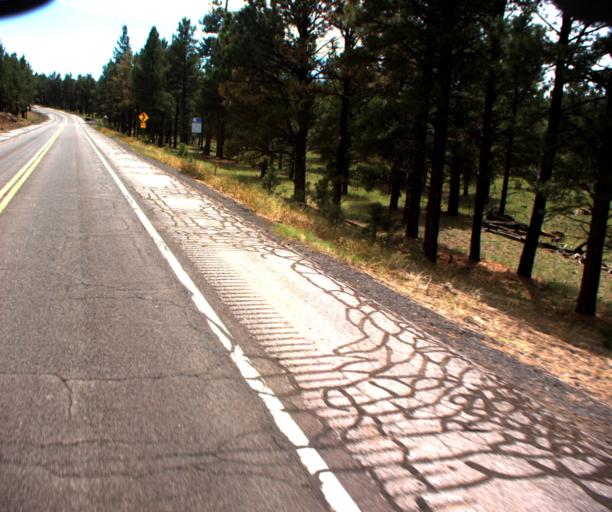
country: US
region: Arizona
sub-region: Coconino County
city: Parks
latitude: 35.4357
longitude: -111.7628
